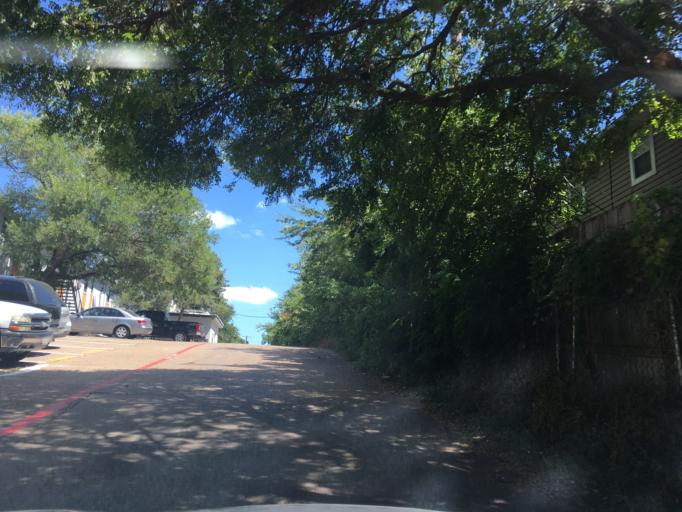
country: US
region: Texas
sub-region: Dallas County
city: Garland
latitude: 32.8433
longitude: -96.6953
